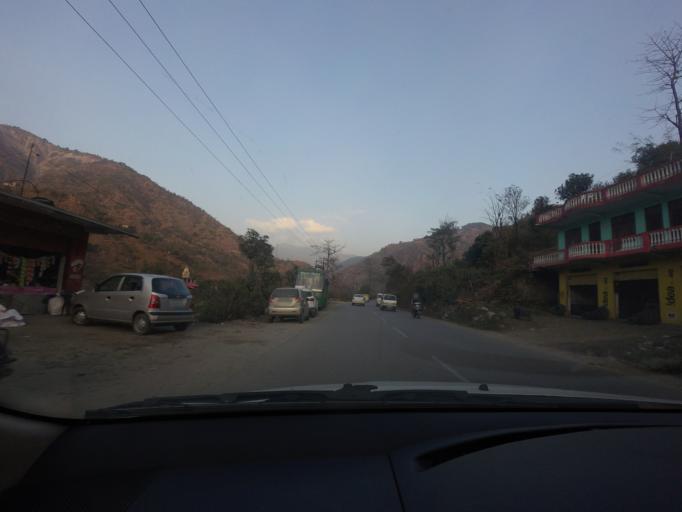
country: IN
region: Himachal Pradesh
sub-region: Mandi
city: Mandi
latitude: 31.7015
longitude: 76.9663
